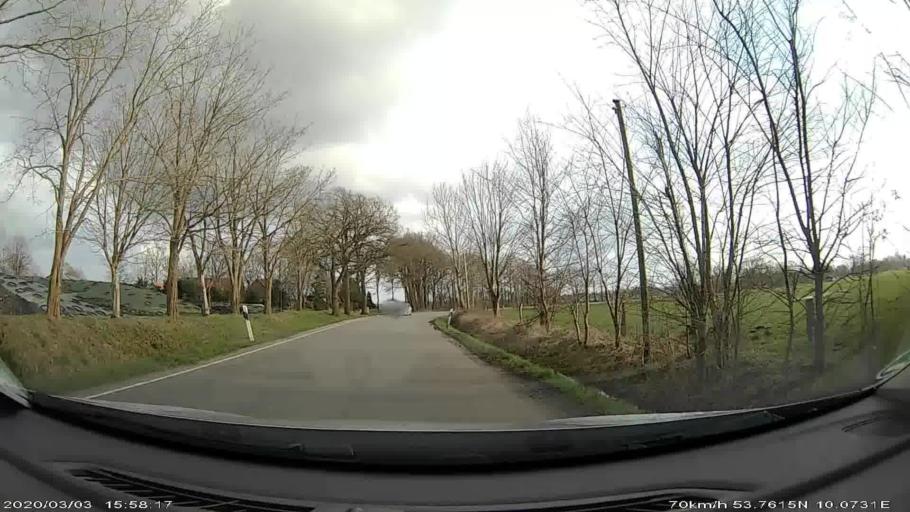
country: DE
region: Schleswig-Holstein
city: Tangstedt
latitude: 53.7626
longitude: 10.0722
